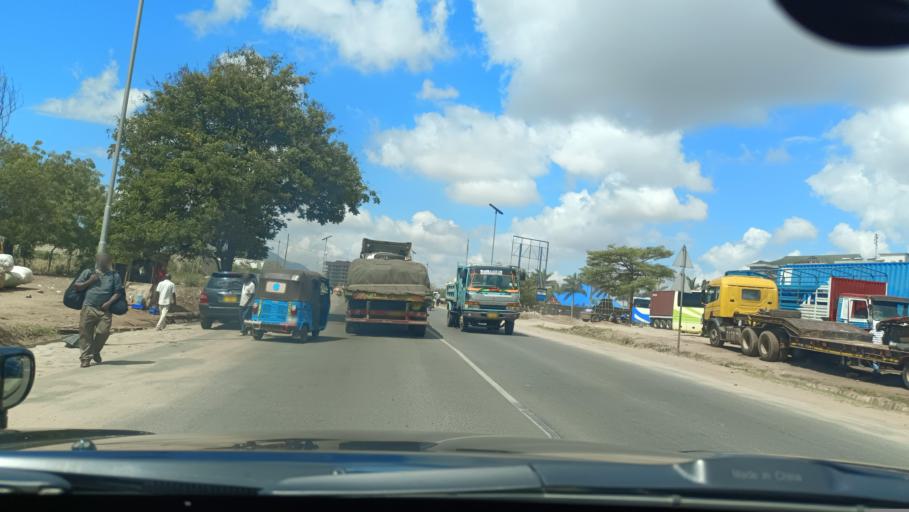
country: TZ
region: Morogoro
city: Morogoro
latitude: -6.8053
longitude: 37.6611
